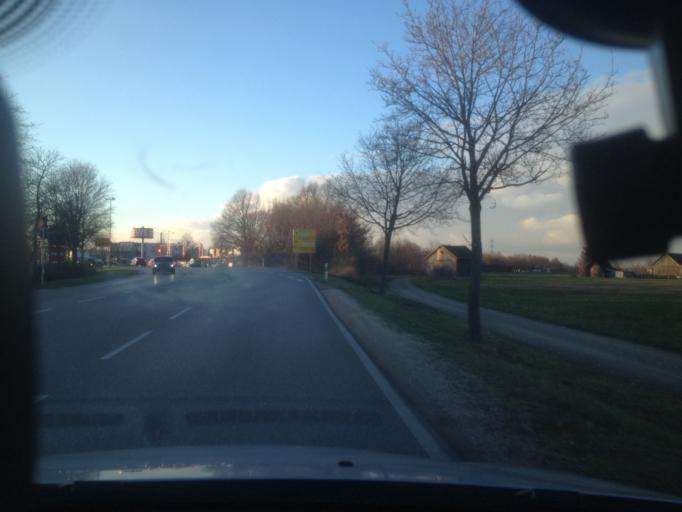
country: DE
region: Bavaria
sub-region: Swabia
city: Mering
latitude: 48.2744
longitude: 10.9800
